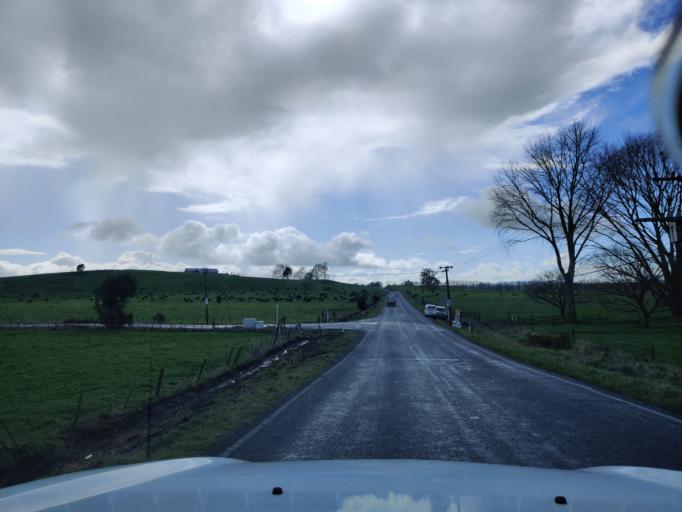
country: NZ
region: Waikato
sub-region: Waikato District
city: Ngaruawahia
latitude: -37.5765
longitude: 175.2350
